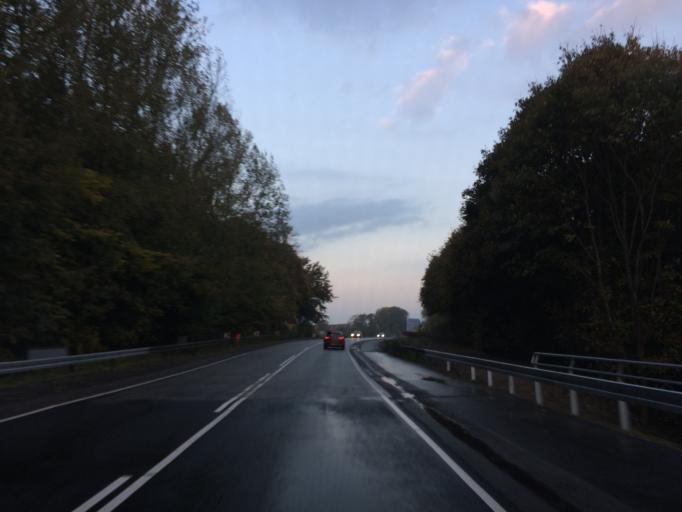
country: DK
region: Zealand
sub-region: Ringsted Kommune
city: Ringsted
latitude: 55.4675
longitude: 11.7540
